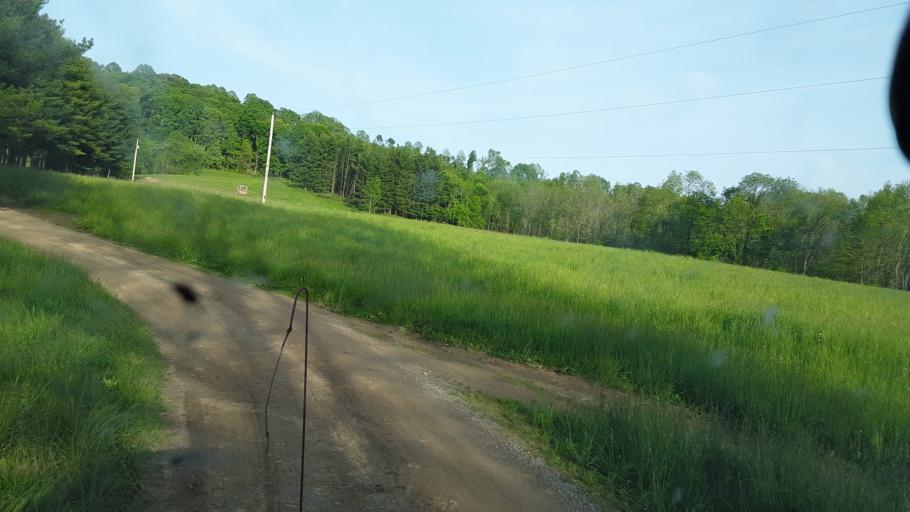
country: US
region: Ohio
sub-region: Fairfield County
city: Lancaster
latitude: 39.5183
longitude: -82.6933
